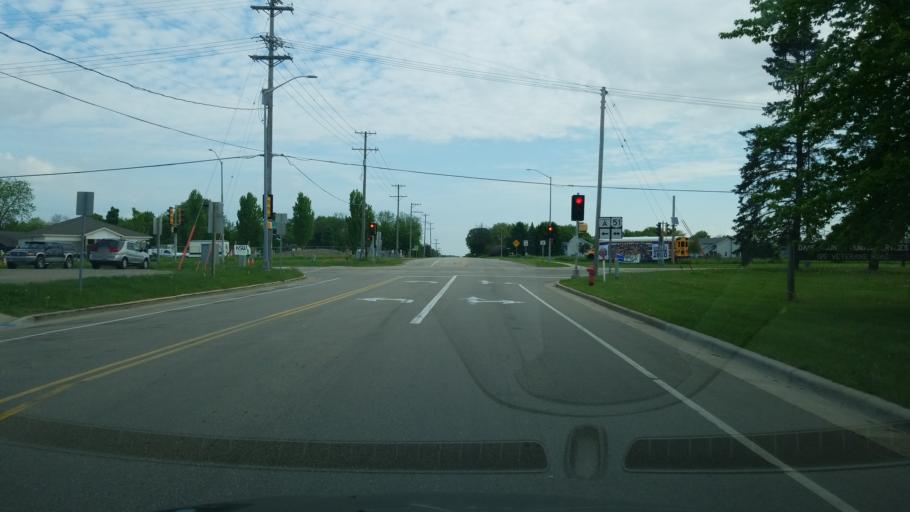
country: US
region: Wisconsin
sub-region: Dane County
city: Stoughton
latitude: 42.9181
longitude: -89.2006
